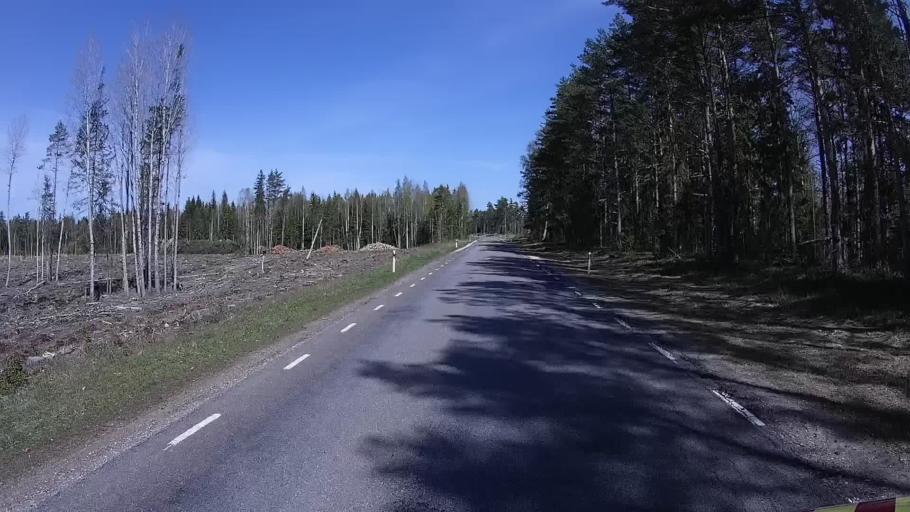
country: EE
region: Harju
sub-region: Nissi vald
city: Turba
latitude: 59.1162
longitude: 24.0559
